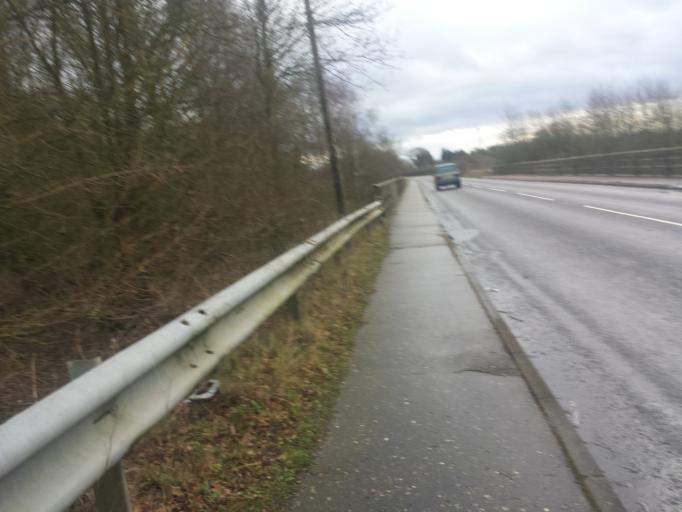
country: GB
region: England
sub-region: Essex
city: Alresford
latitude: 51.8856
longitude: 1.0314
